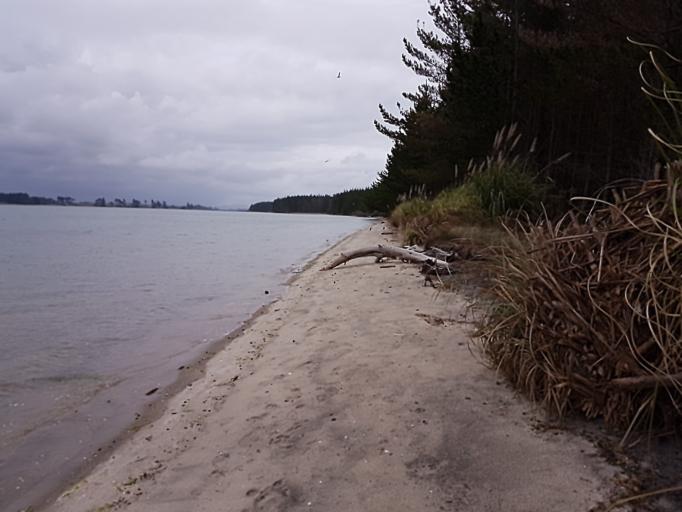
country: NZ
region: Bay of Plenty
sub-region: Tauranga City
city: Tauranga
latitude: -37.6384
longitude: 176.1424
